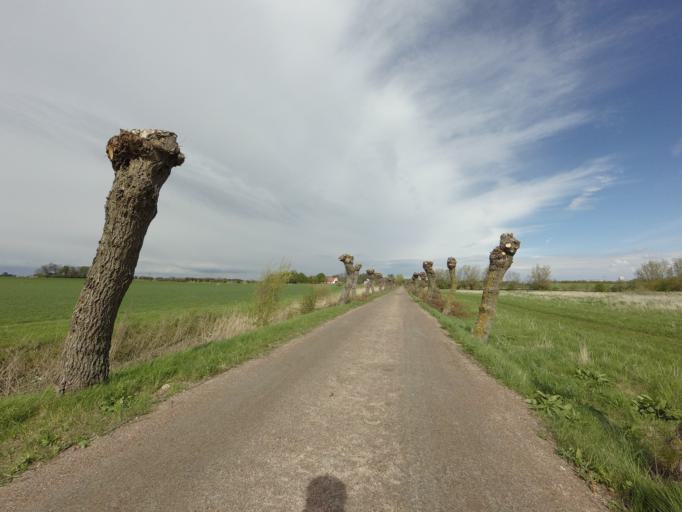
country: SE
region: Skane
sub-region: Malmo
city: Bunkeflostrand
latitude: 55.5430
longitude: 12.9697
